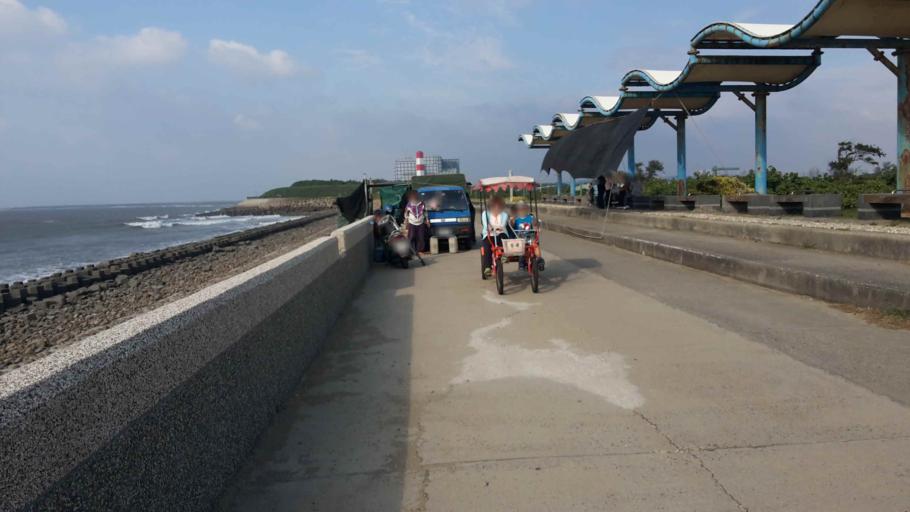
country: TW
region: Taiwan
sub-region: Hsinchu
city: Hsinchu
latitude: 24.8248
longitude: 120.9103
